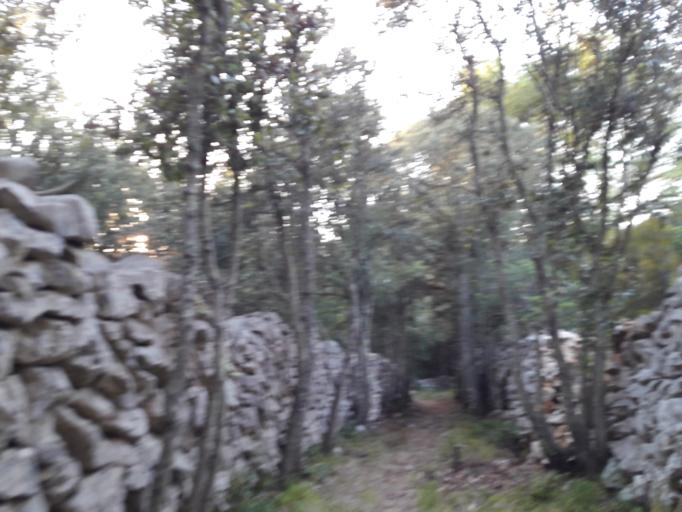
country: HR
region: Licko-Senjska
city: Novalja
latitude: 44.3623
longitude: 14.6968
